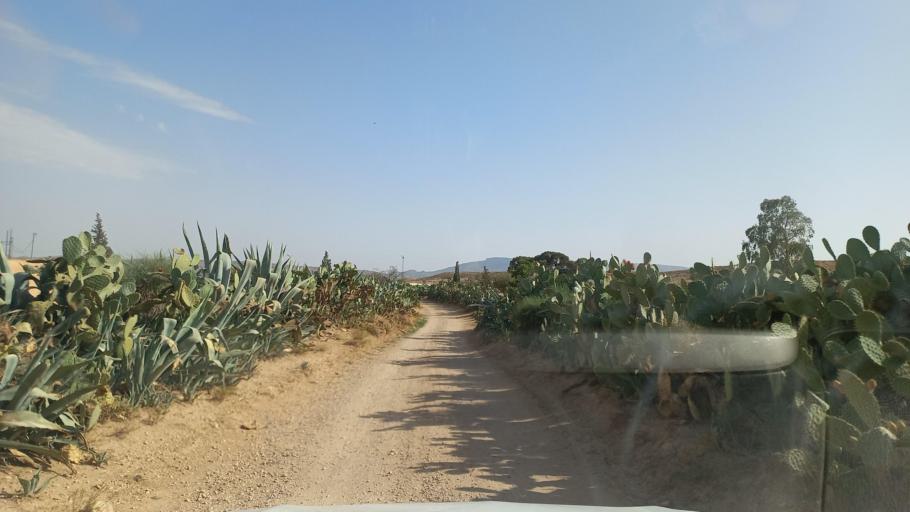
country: TN
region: Al Qasrayn
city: Kasserine
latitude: 35.2531
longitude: 8.9286
